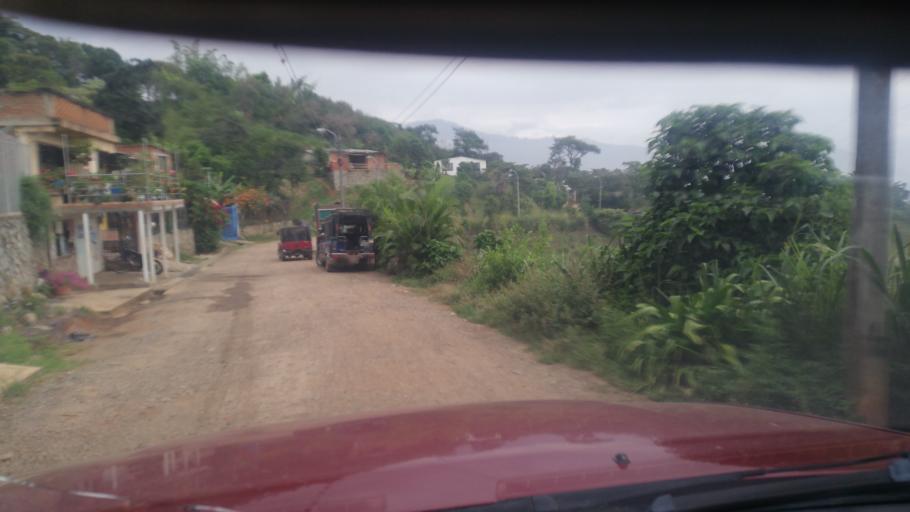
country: CO
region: Valle del Cauca
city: Cali
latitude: 3.5076
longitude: -76.5420
